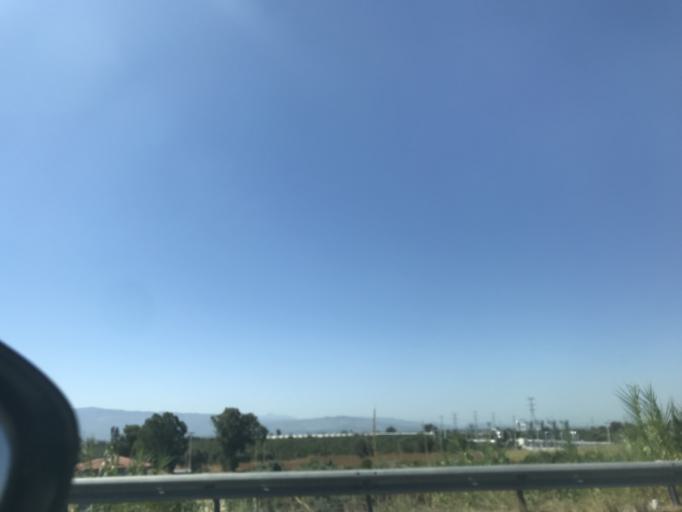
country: TR
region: Aydin
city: Germencik
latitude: 37.8711
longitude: 27.6342
